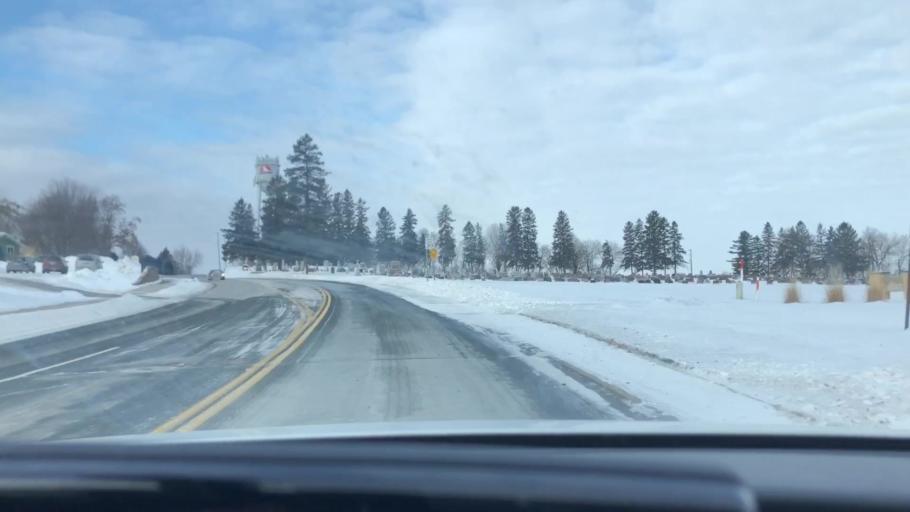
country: US
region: Minnesota
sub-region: Carver County
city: Waconia
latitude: 44.8505
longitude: -93.7757
